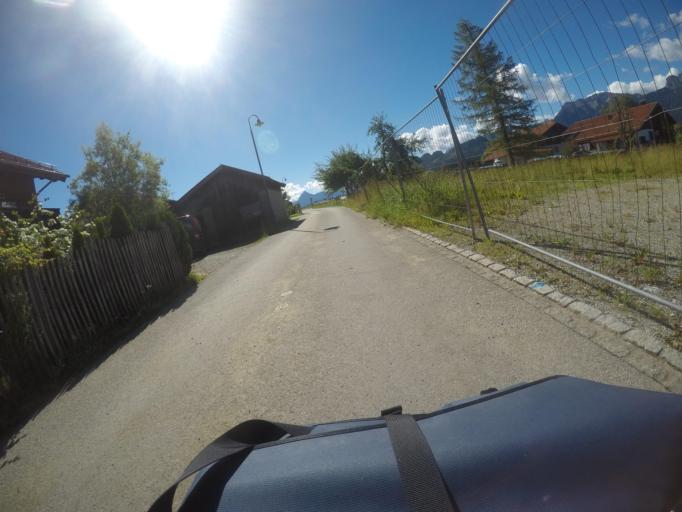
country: DE
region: Bavaria
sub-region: Swabia
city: Pfronten
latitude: 47.5969
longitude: 10.5682
